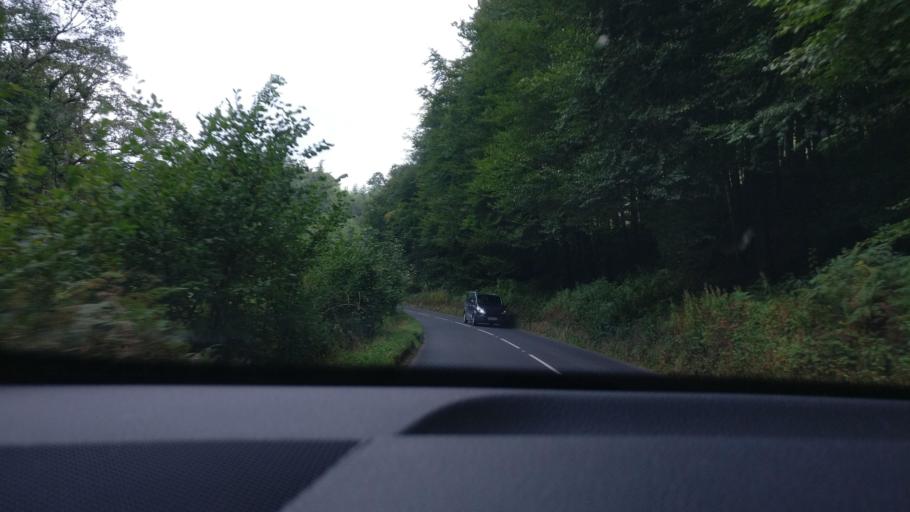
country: GB
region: England
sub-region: Devon
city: South Molton
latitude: 51.0701
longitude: -3.8634
